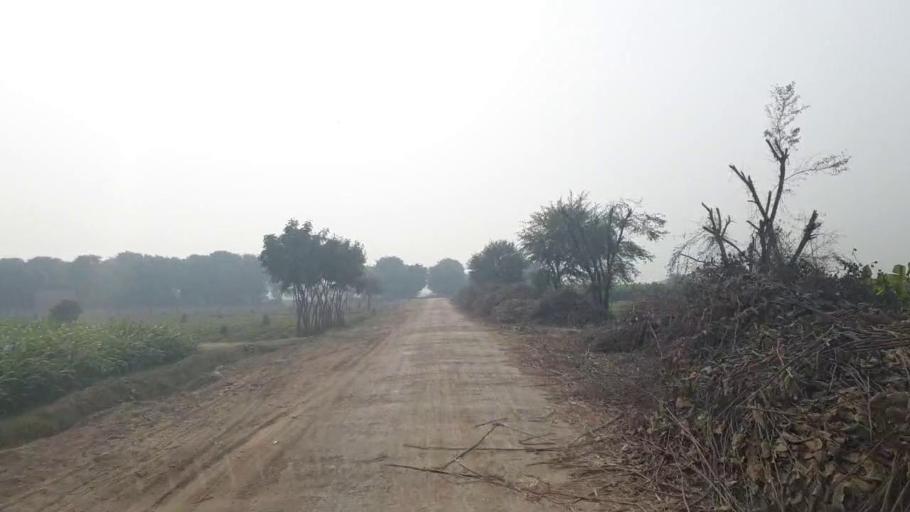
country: PK
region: Sindh
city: Tando Adam
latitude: 25.7131
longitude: 68.6263
